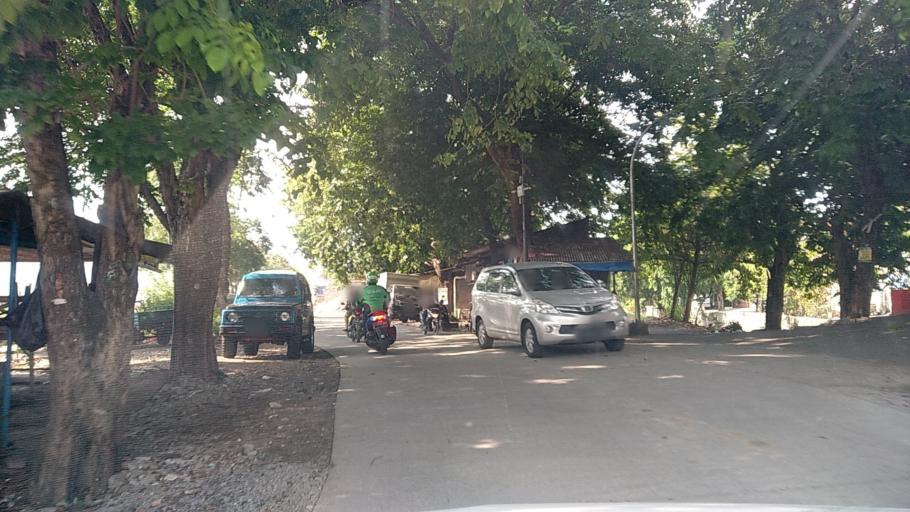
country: ID
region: Central Java
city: Semarang
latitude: -6.9834
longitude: 110.4373
